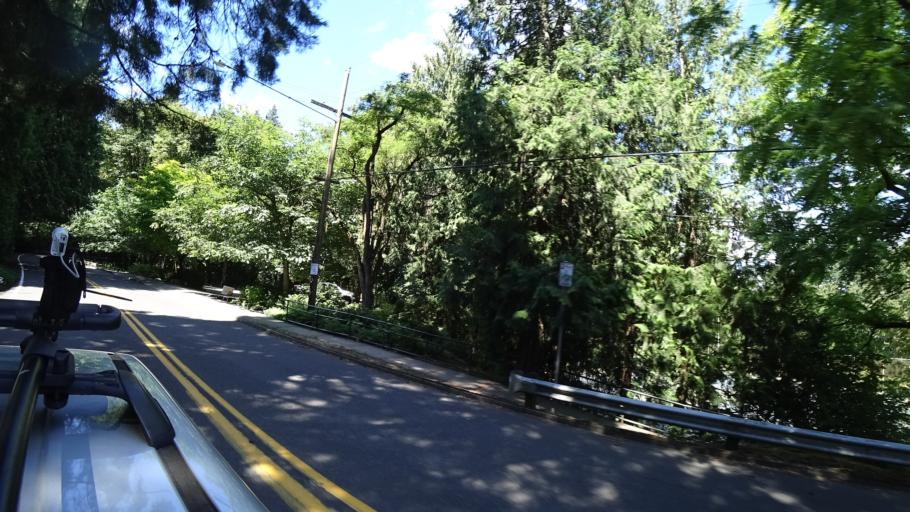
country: US
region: Oregon
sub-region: Multnomah County
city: Portland
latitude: 45.5036
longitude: -122.7078
